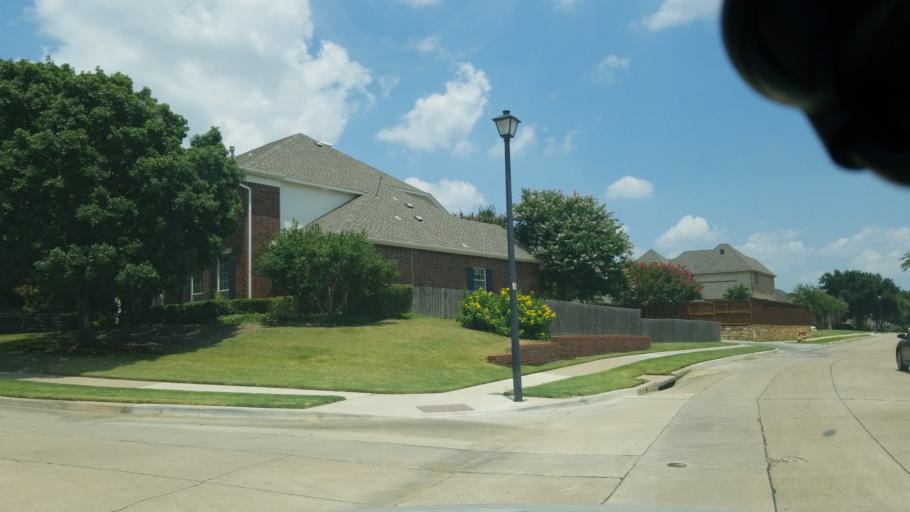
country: US
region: Texas
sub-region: Dallas County
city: Carrollton
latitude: 32.9699
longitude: -96.8811
